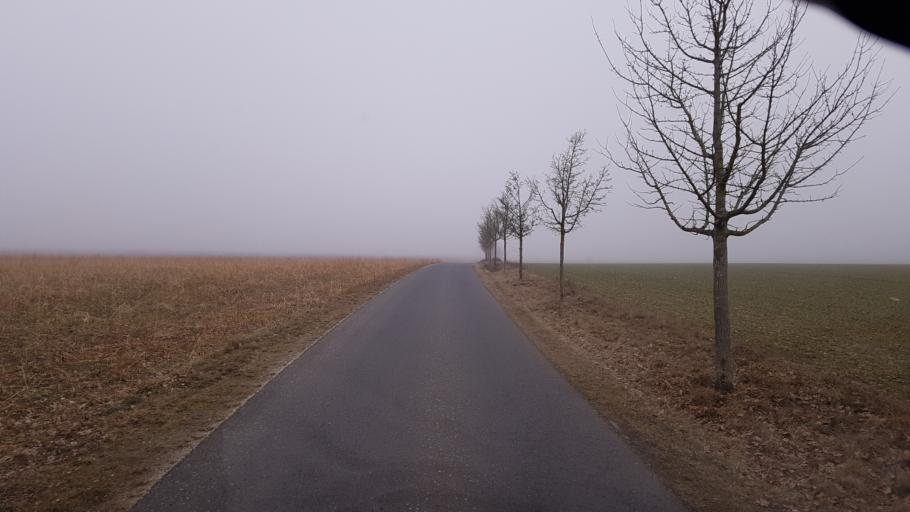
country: DE
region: Brandenburg
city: Ihlow
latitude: 51.8638
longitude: 13.2150
